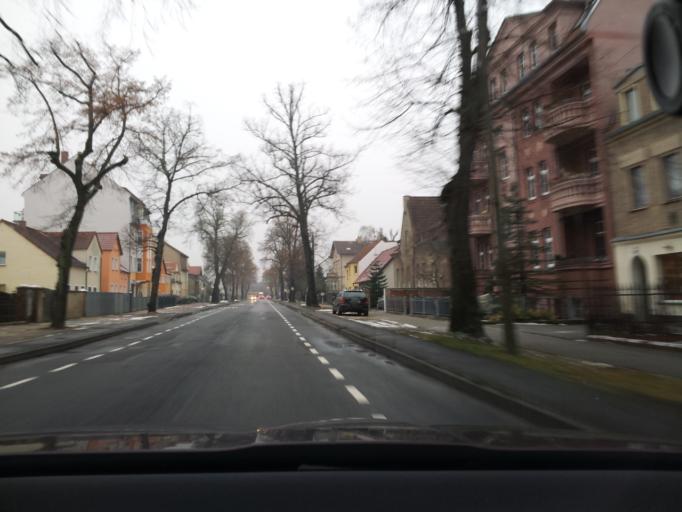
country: DE
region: Brandenburg
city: Furstenwalde
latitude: 52.3563
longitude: 14.0730
